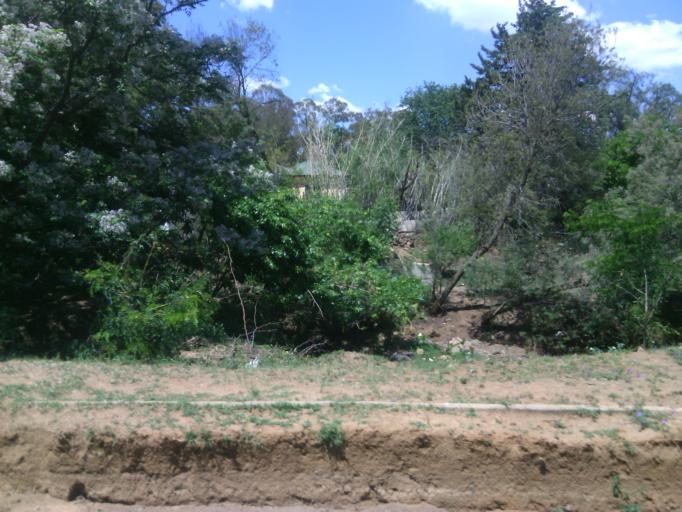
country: ZA
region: Orange Free State
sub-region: Xhariep District Municipality
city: Dewetsdorp
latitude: -29.5888
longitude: 26.6649
